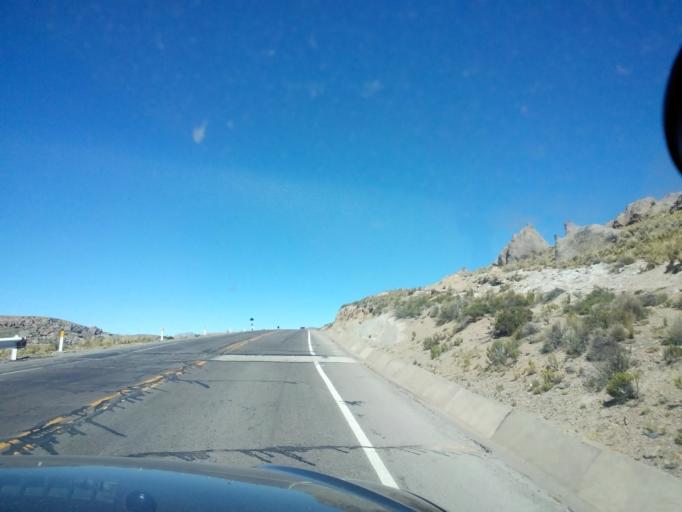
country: PE
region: Arequipa
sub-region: Provincia de Caylloma
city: Vizcachane
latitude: -15.9302
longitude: -71.1895
